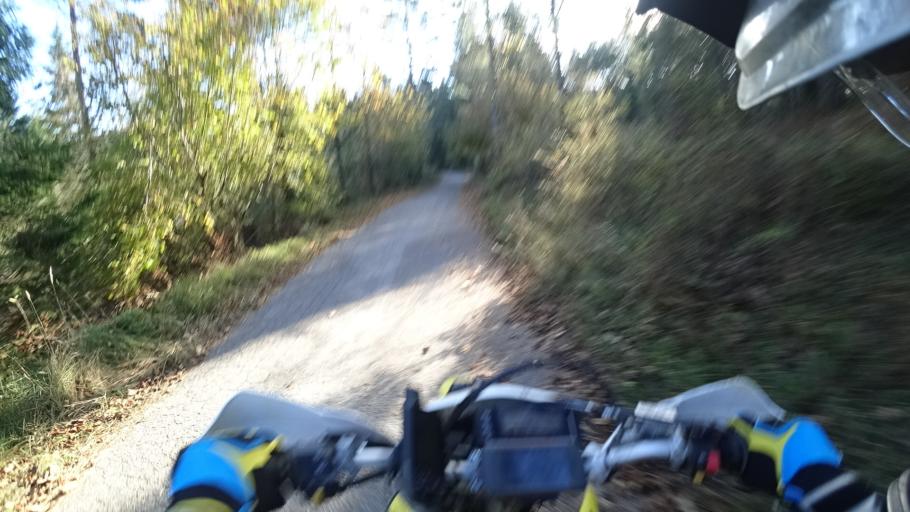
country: HR
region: Karlovacka
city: Plaski
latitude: 44.9843
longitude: 15.4174
